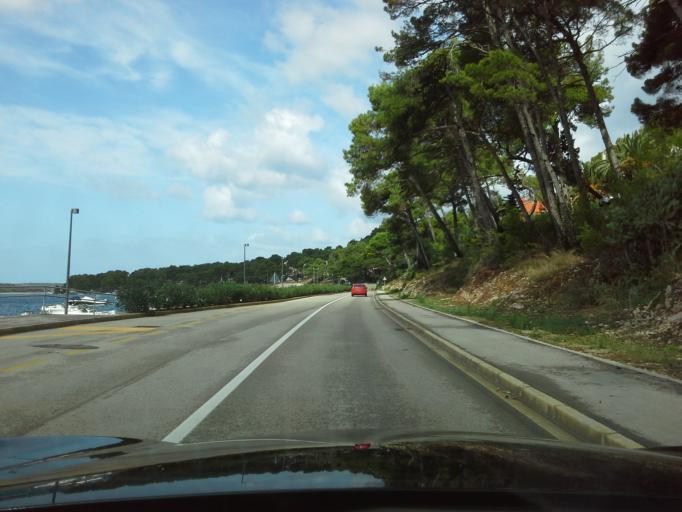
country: HR
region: Primorsko-Goranska
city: Mali Losinj
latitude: 44.5508
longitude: 14.4502
